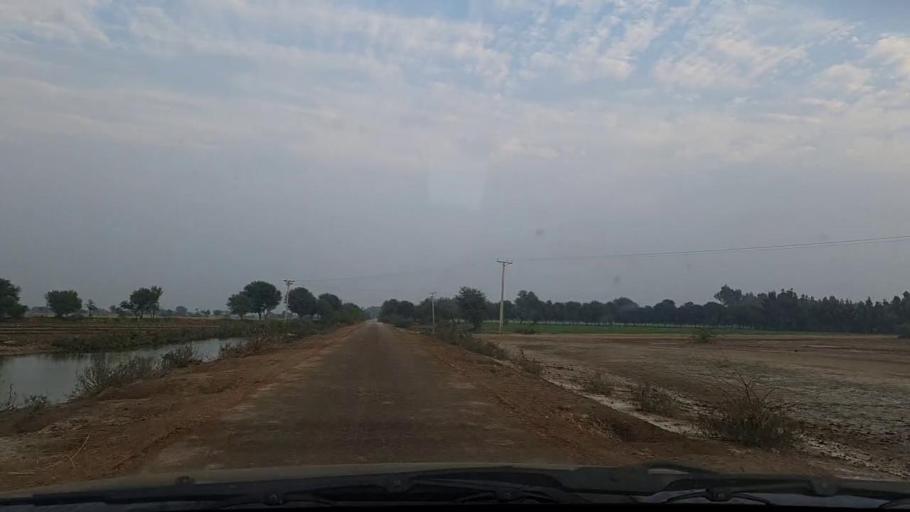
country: PK
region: Sindh
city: Pithoro
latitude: 25.6022
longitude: 69.4556
